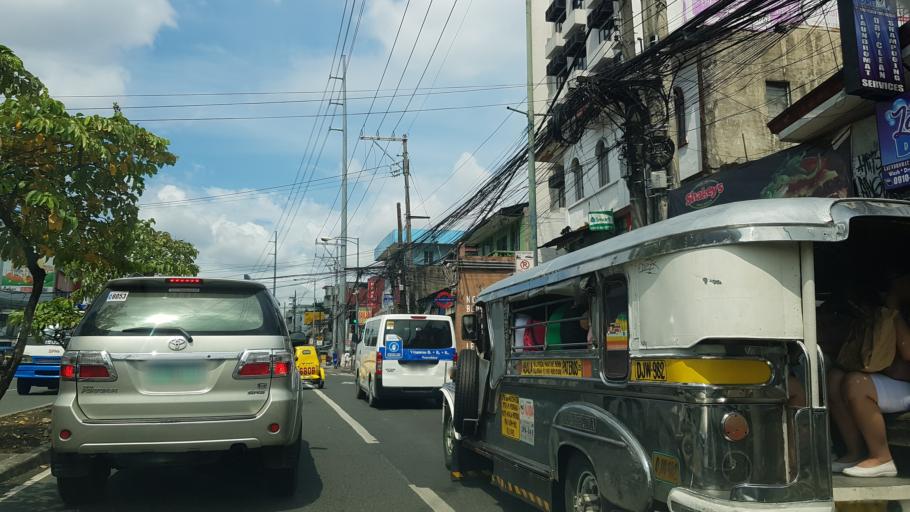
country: PH
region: Metro Manila
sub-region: Makati City
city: Makati City
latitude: 14.5584
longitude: 121.0459
